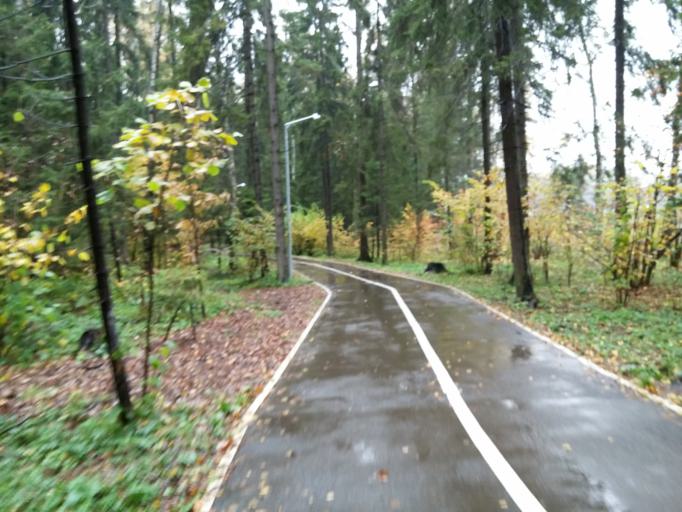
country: RU
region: Moskovskaya
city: Selyatino
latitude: 55.5175
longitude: 36.9895
